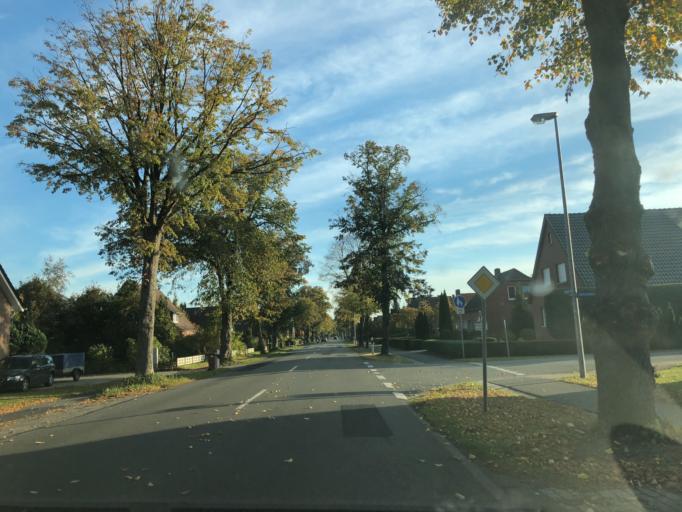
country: DE
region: Lower Saxony
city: Papenburg
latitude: 53.0621
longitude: 7.3578
